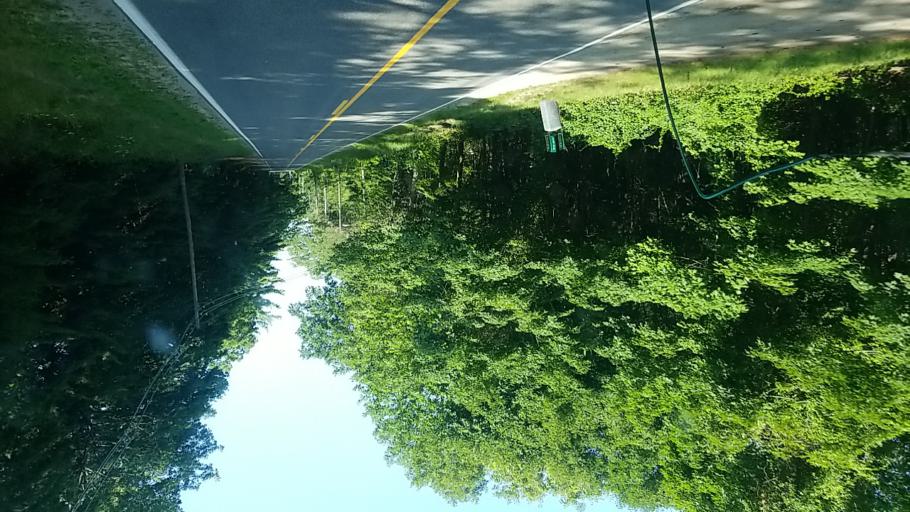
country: US
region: Michigan
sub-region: Muskegon County
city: Montague
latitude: 43.3493
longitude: -86.4082
